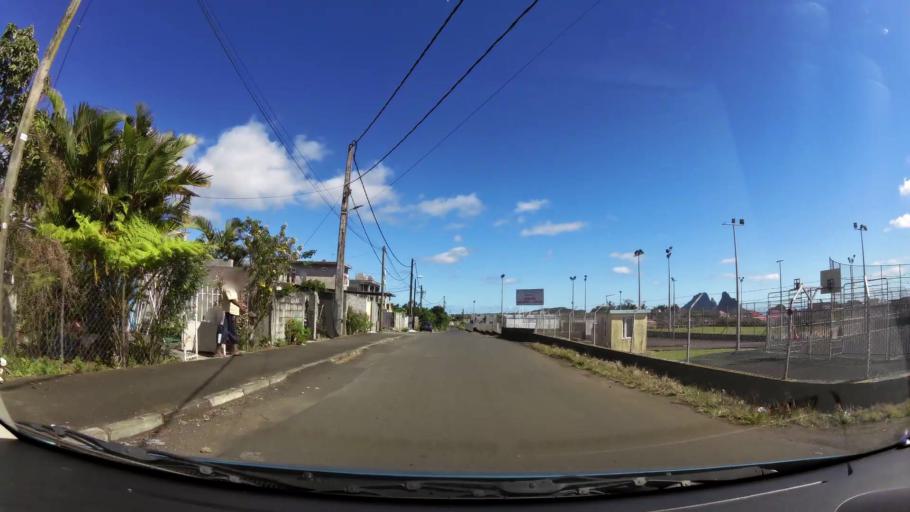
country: MU
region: Plaines Wilhems
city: Vacoas
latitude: -20.3284
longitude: 57.4846
